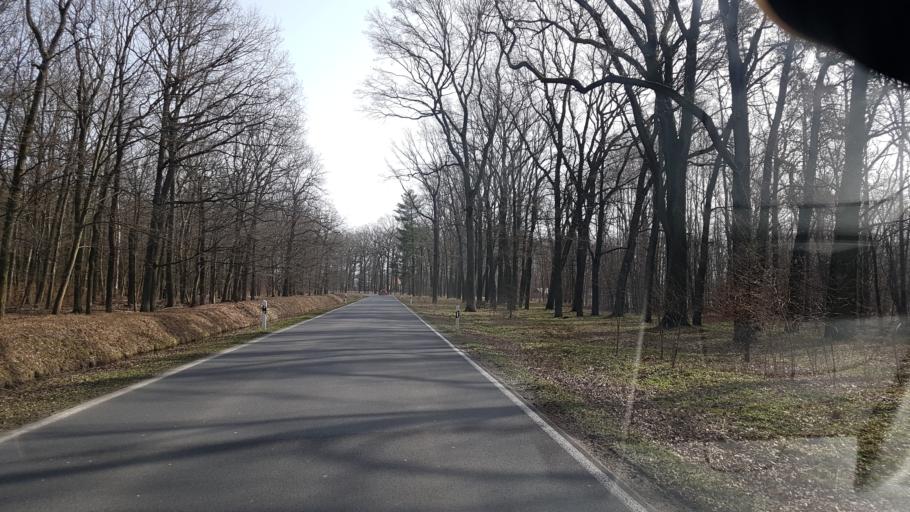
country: DE
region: Brandenburg
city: Cottbus
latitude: 51.7393
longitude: 14.3584
